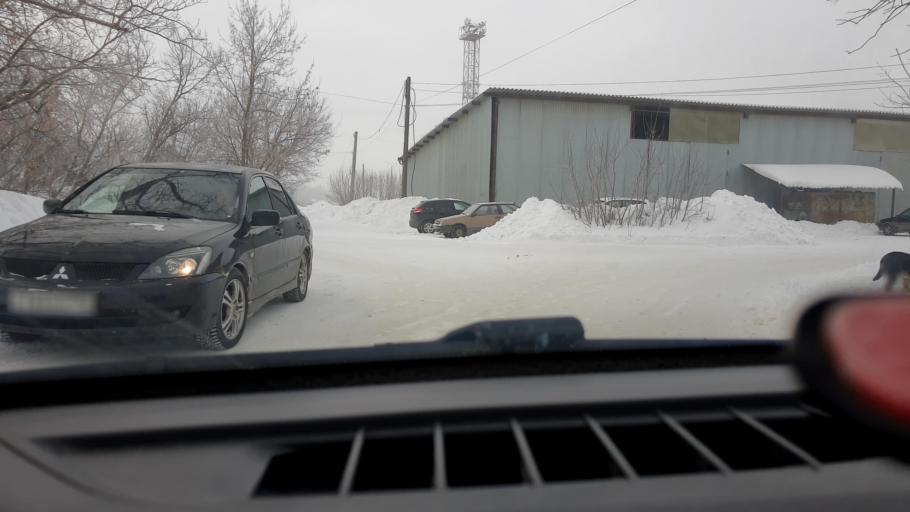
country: RU
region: Nizjnij Novgorod
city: Babino
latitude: 56.2623
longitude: 43.6022
